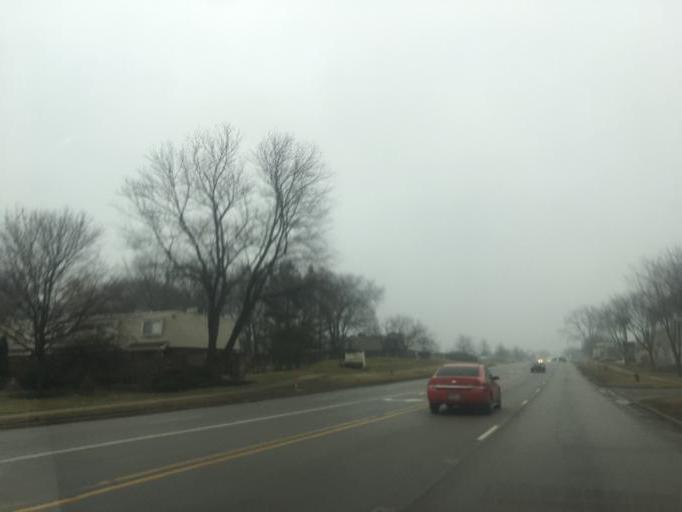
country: US
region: Illinois
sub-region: DuPage County
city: Lisle
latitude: 41.7971
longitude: -88.1037
